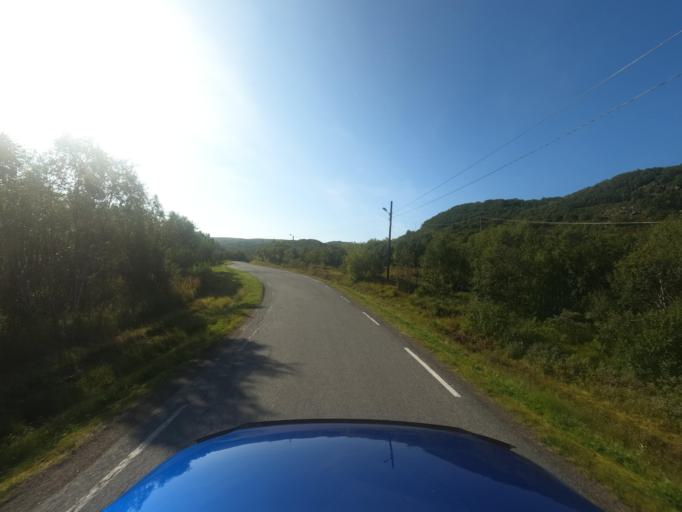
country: NO
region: Nordland
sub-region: Vestvagoy
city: Evjen
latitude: 68.2965
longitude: 13.8666
